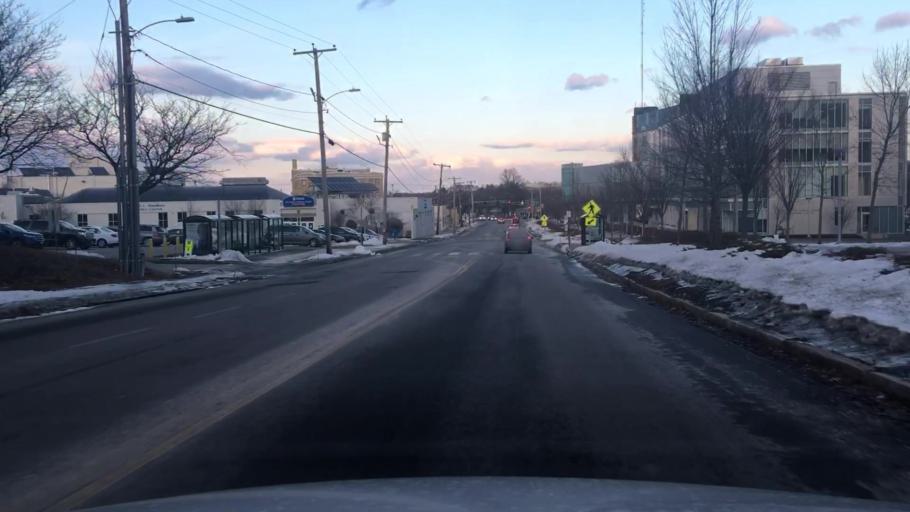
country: US
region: Maine
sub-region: Cumberland County
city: Portland
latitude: 43.6619
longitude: -70.2752
